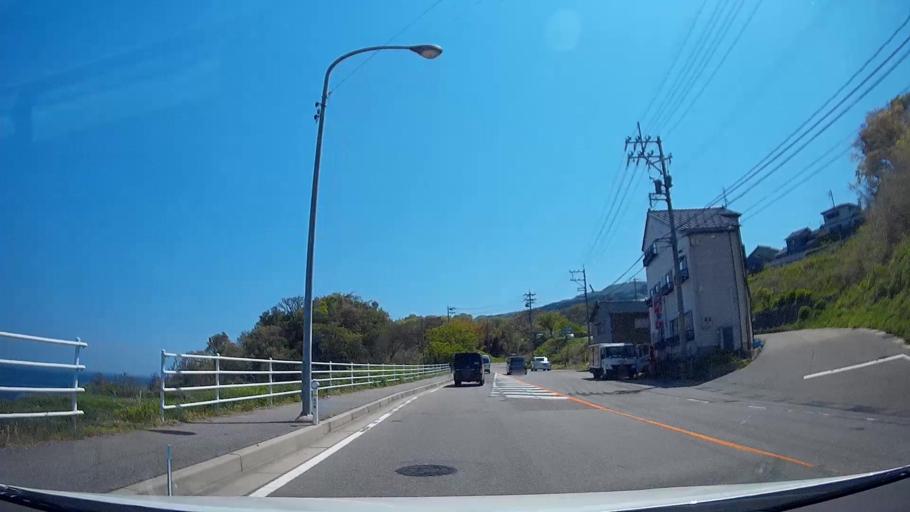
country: JP
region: Ishikawa
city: Nanao
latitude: 37.3972
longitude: 136.9310
